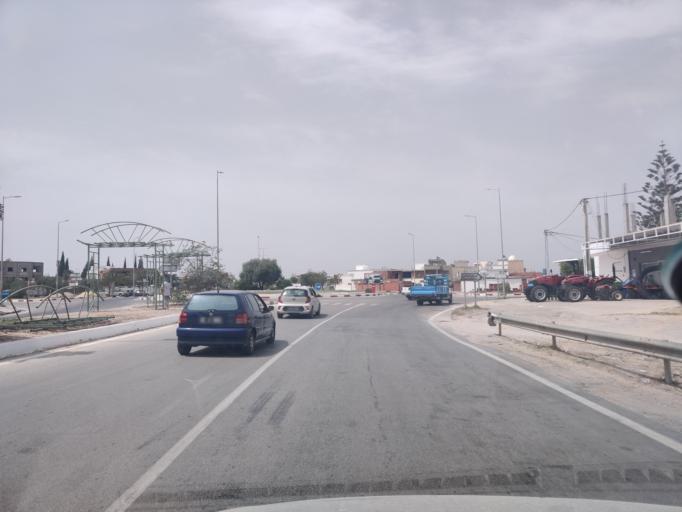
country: TN
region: Susah
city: Akouda
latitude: 35.8354
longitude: 10.5597
